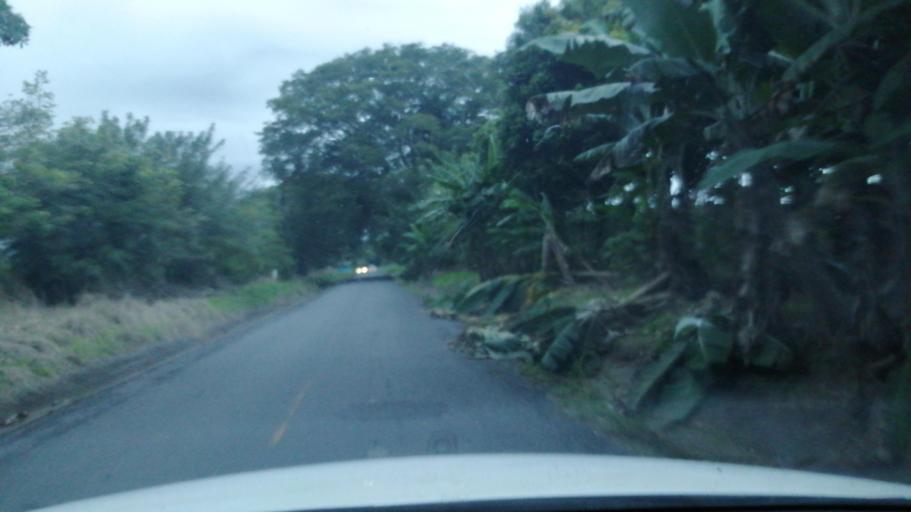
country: PA
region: Chiriqui
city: Alanje
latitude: 8.3969
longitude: -82.4966
